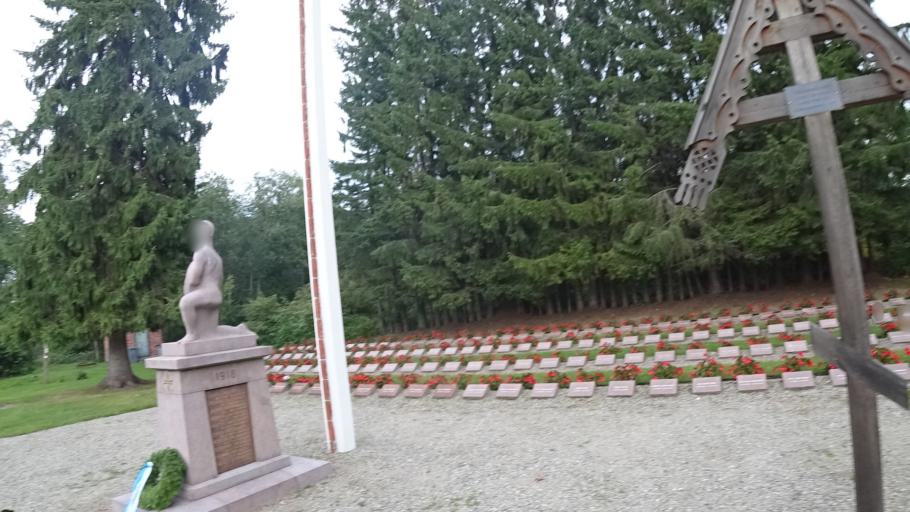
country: FI
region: North Karelia
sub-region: Joensuu
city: Ilomantsi
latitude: 62.6776
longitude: 30.9174
